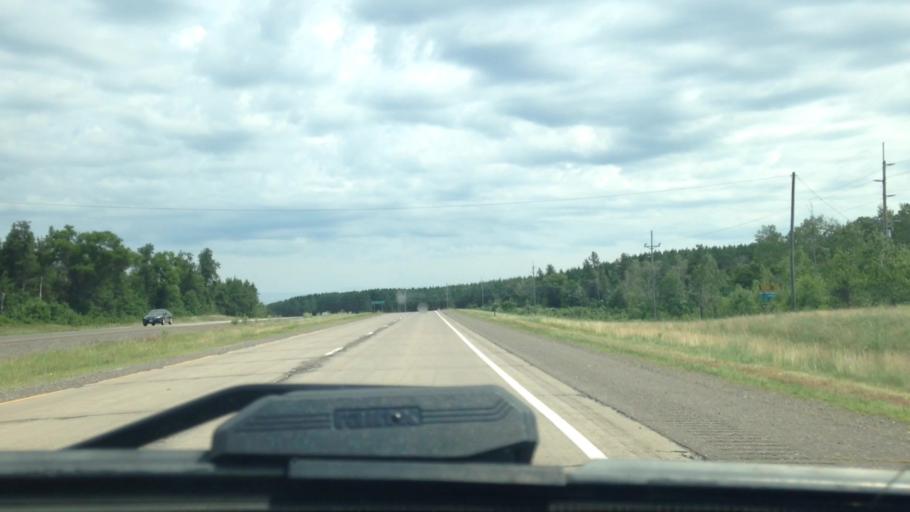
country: US
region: Wisconsin
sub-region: Douglas County
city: Lake Nebagamon
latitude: 46.1797
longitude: -91.8014
